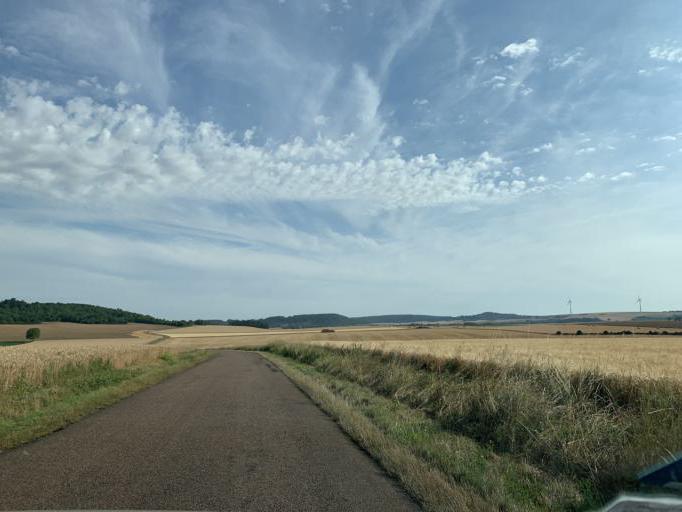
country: FR
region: Bourgogne
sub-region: Departement de la Nievre
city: Clamecy
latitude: 47.4558
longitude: 3.4244
